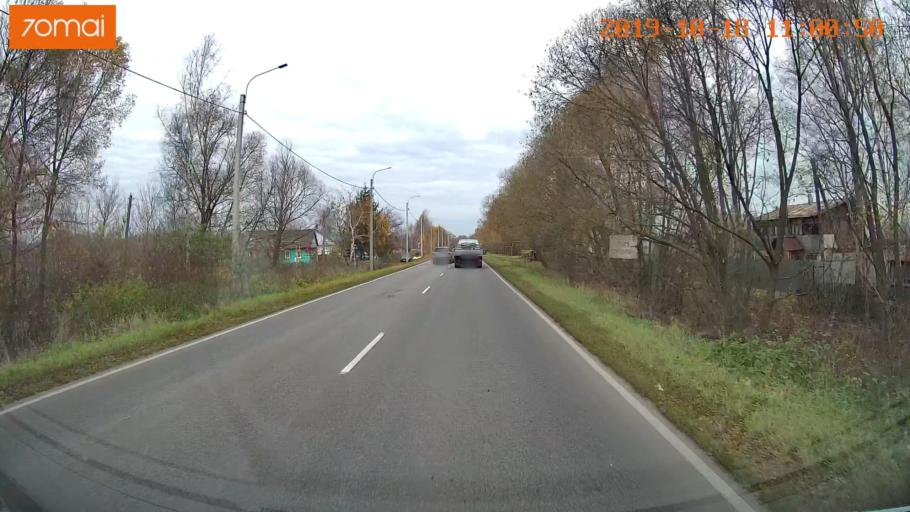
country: RU
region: Tula
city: Yepifan'
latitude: 53.8477
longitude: 38.5528
